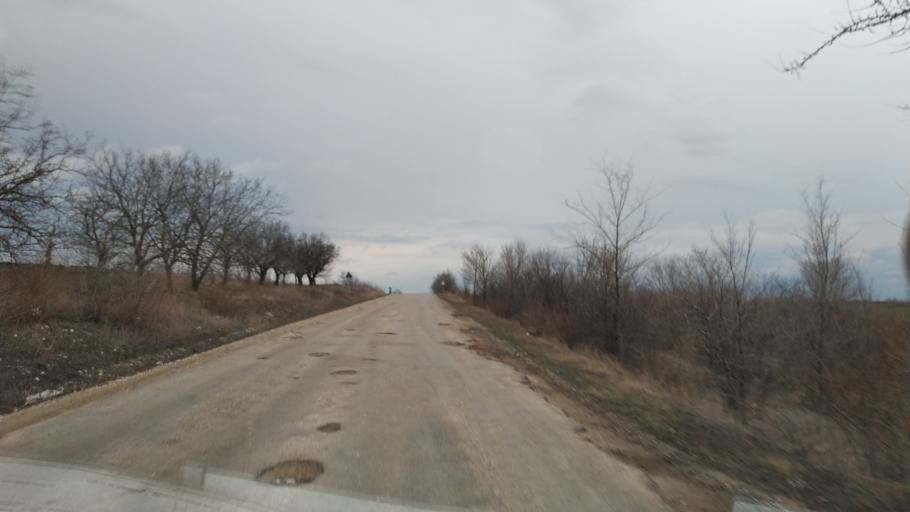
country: MD
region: Causeni
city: Causeni
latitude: 46.6115
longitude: 29.4010
